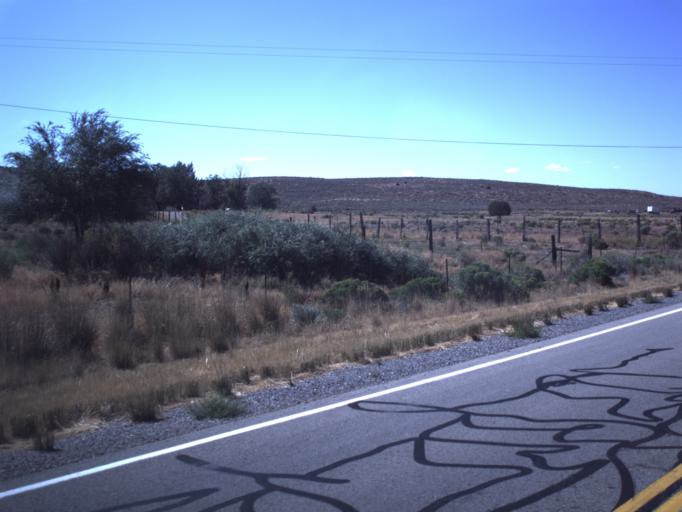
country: US
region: Utah
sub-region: Tooele County
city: Tooele
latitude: 40.4400
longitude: -112.3705
